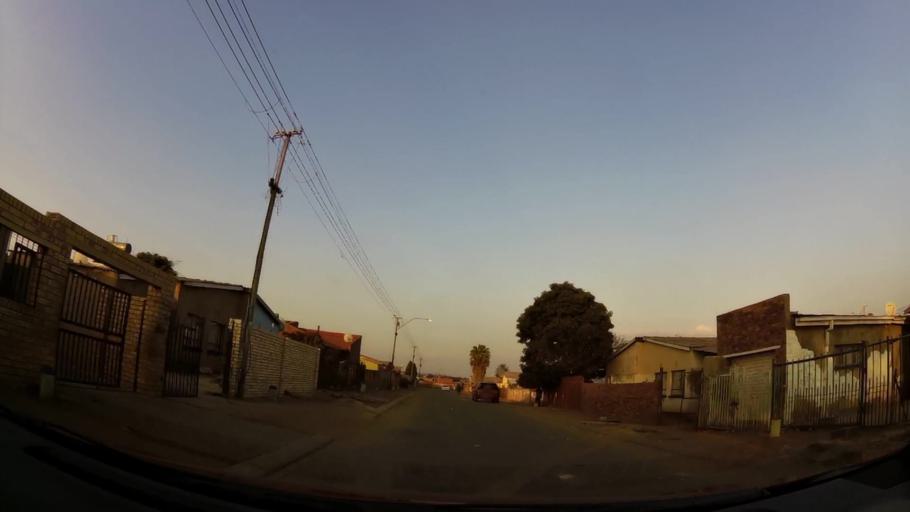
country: ZA
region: Gauteng
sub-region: City of Johannesburg Metropolitan Municipality
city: Soweto
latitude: -26.2901
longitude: 27.8981
